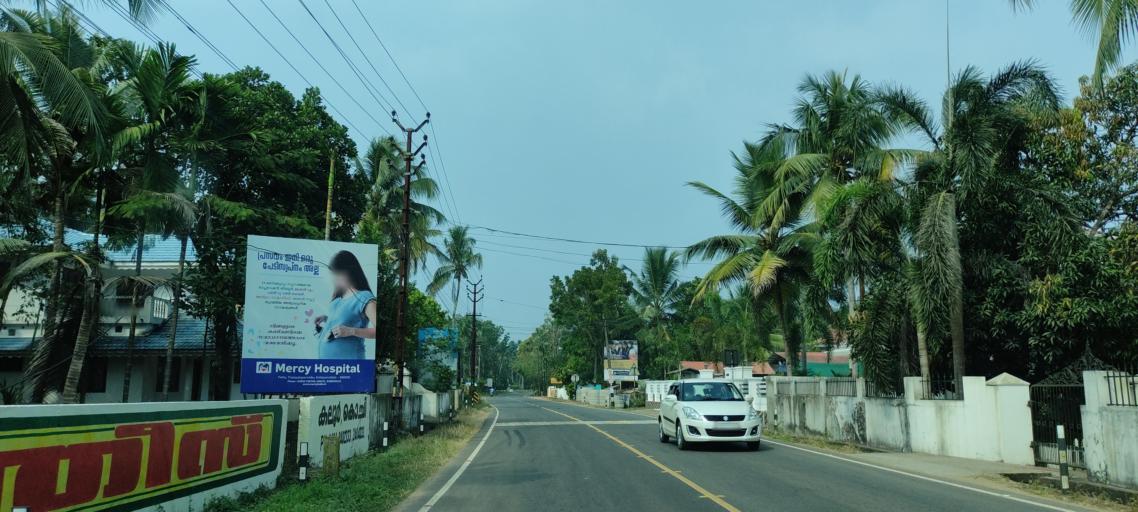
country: IN
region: Kerala
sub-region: Kottayam
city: Vaikam
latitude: 9.7624
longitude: 76.4148
